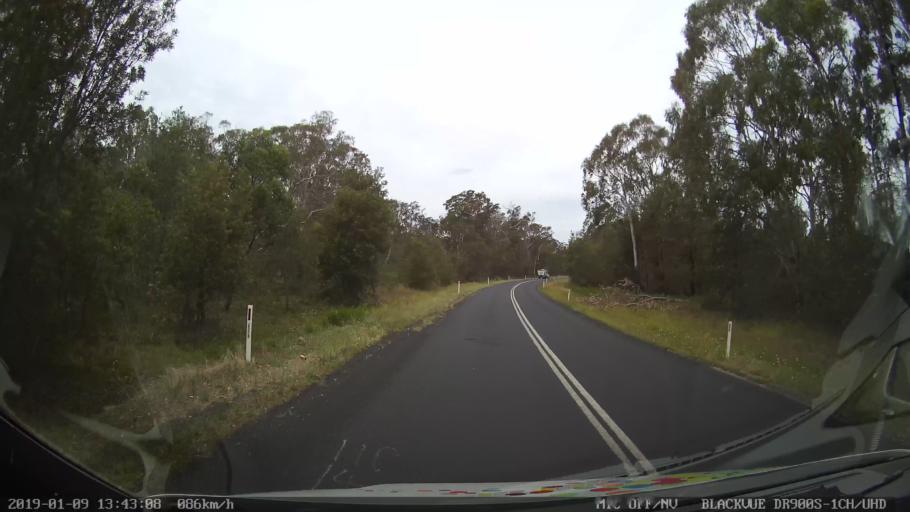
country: AU
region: New South Wales
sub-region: Armidale Dumaresq
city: Enmore
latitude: -30.4909
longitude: 152.1670
